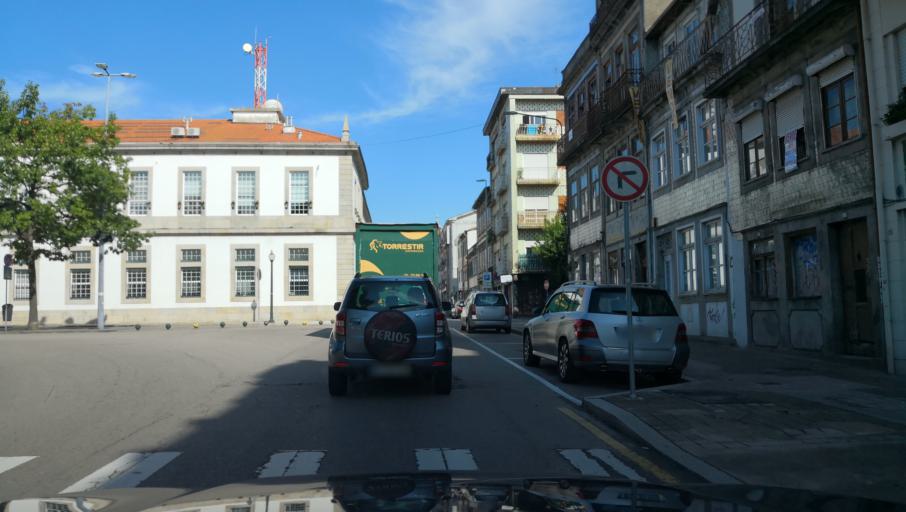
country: PT
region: Porto
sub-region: Porto
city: Porto
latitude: 41.1549
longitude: -8.6120
